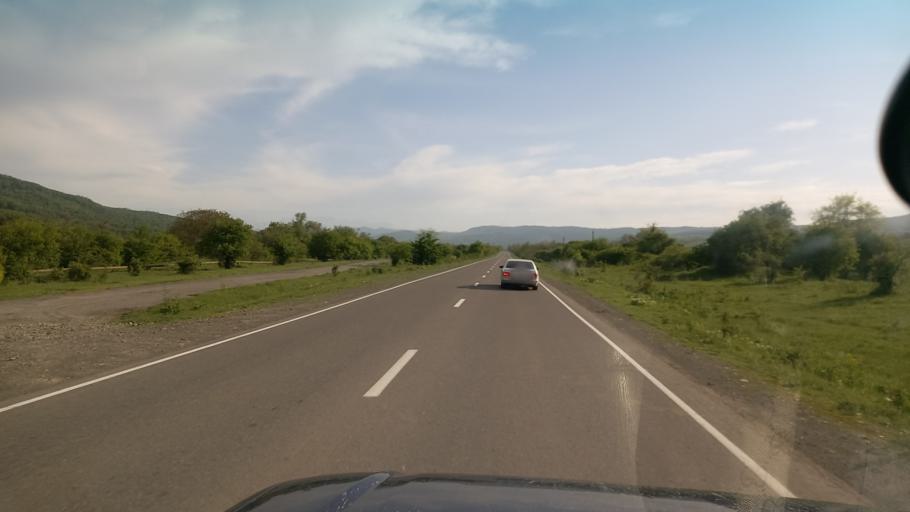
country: RU
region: Ingushetiya
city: Nesterovskaya
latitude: 43.2132
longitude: 45.0230
